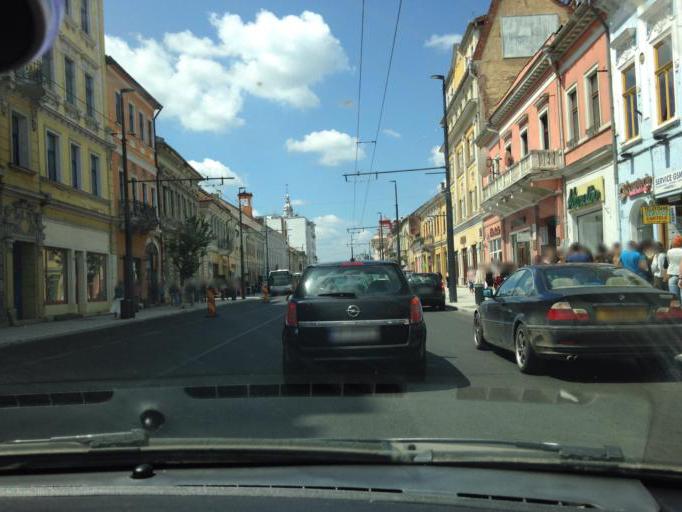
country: RO
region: Cluj
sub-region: Municipiul Cluj-Napoca
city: Cluj-Napoca
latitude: 46.7701
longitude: 23.5880
